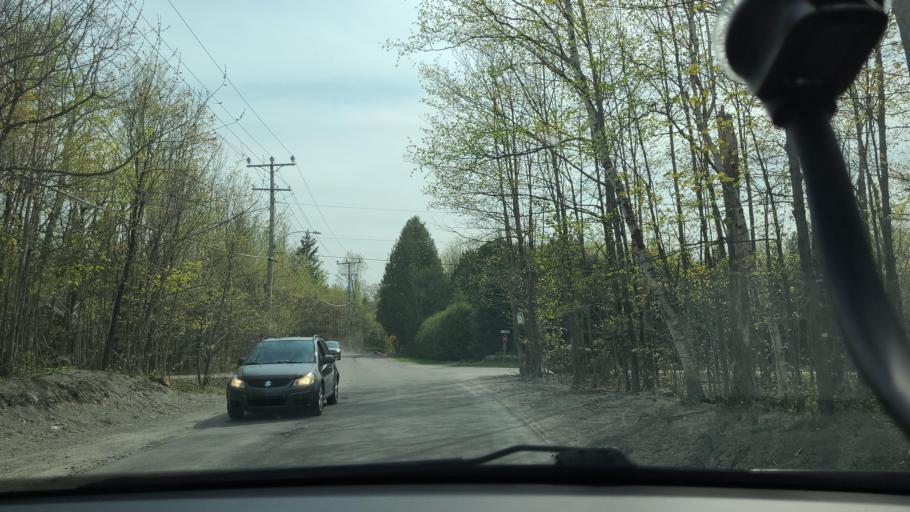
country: CA
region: Quebec
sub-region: Laurentides
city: Prevost
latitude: 45.8949
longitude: -74.0393
